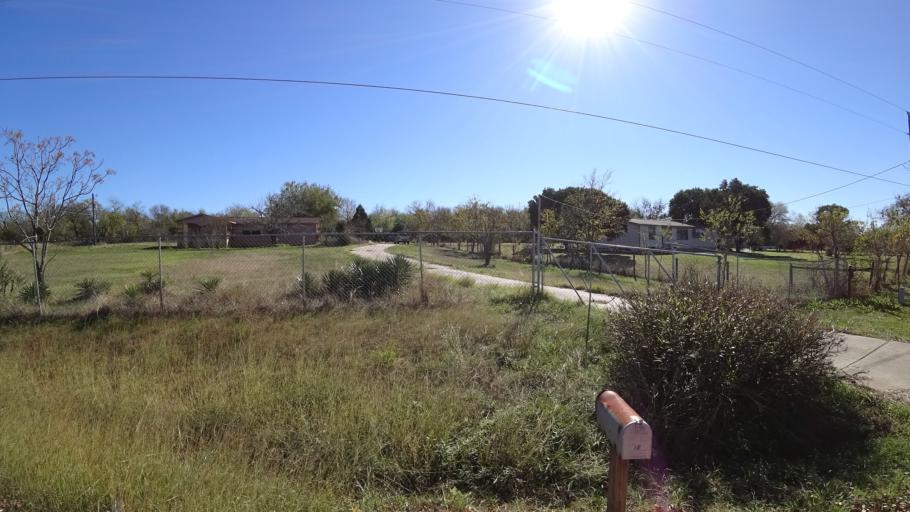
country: US
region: Texas
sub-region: Travis County
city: Garfield
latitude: 30.1091
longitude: -97.5949
